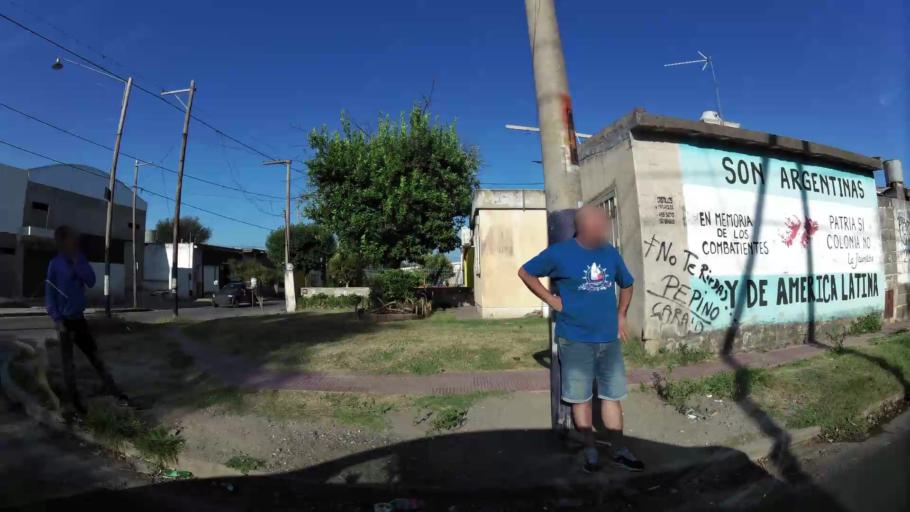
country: AR
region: Cordoba
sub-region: Departamento de Capital
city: Cordoba
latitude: -31.4411
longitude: -64.2480
